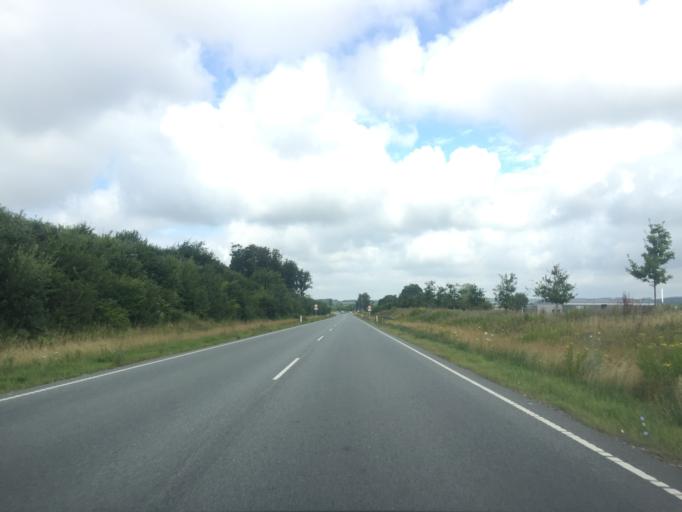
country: DK
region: South Denmark
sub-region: Svendborg Kommune
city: Thuro By
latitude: 55.0786
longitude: 10.6453
